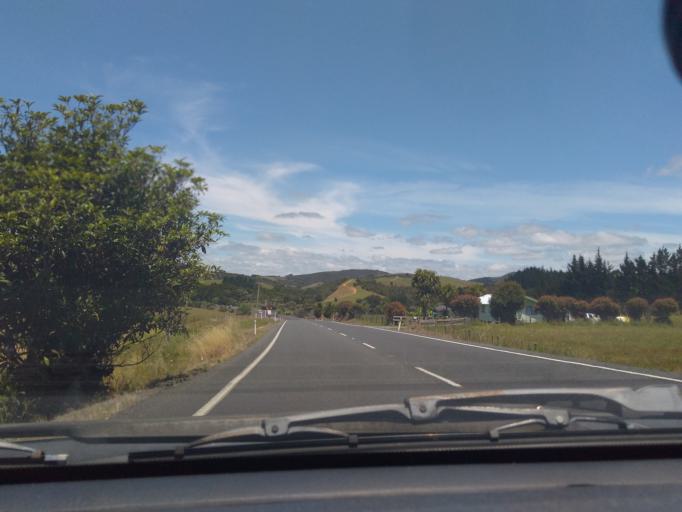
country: NZ
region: Northland
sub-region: Far North District
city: Taipa
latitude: -35.0113
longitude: 173.6223
